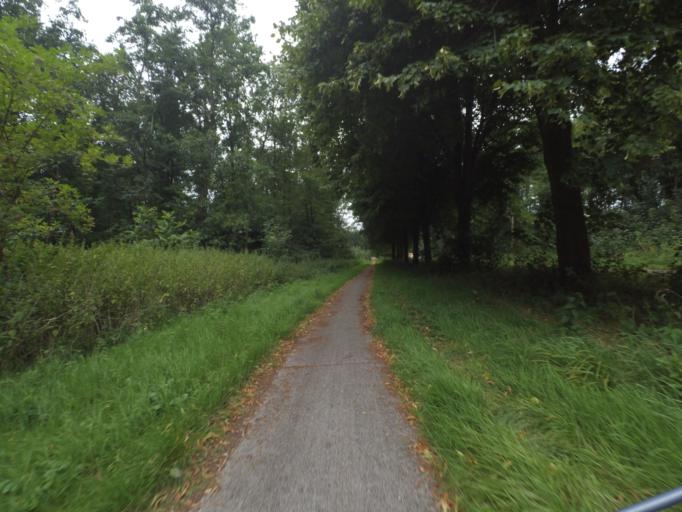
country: NL
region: Flevoland
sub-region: Gemeente Lelystad
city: Lelystad
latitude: 52.4556
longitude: 5.4352
